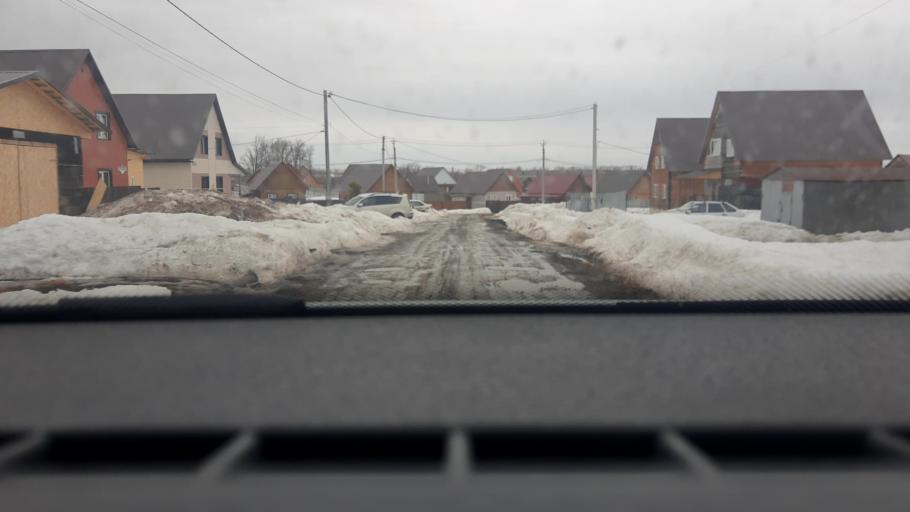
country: RU
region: Bashkortostan
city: Iglino
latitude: 54.8267
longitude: 56.4337
